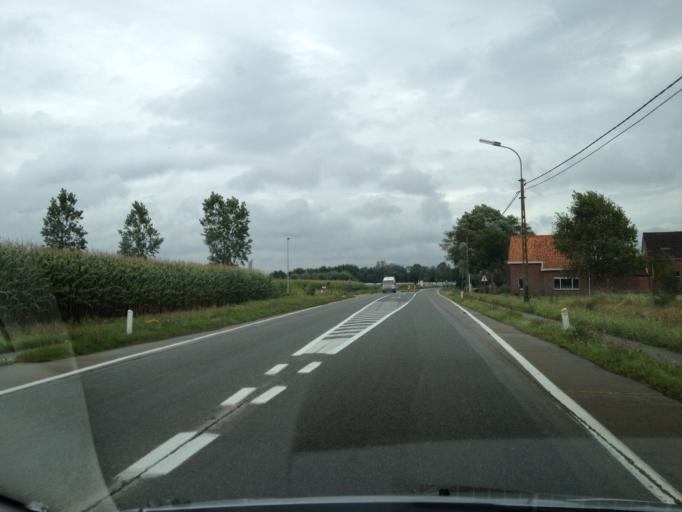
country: BE
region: Flanders
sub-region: Provincie West-Vlaanderen
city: Ichtegem
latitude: 51.1197
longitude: 3.0215
